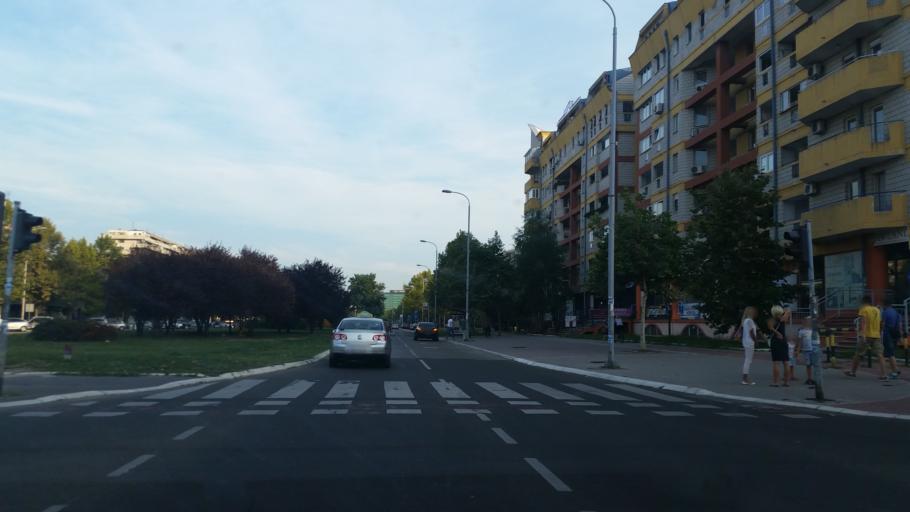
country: RS
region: Central Serbia
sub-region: Belgrade
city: Novi Beograd
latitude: 44.8143
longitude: 20.4251
